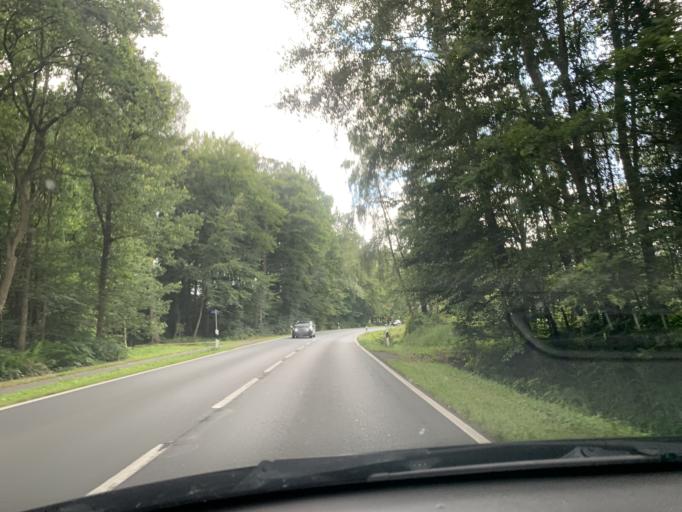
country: DE
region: Lower Saxony
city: Bad Zwischenahn
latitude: 53.2070
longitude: 8.0057
